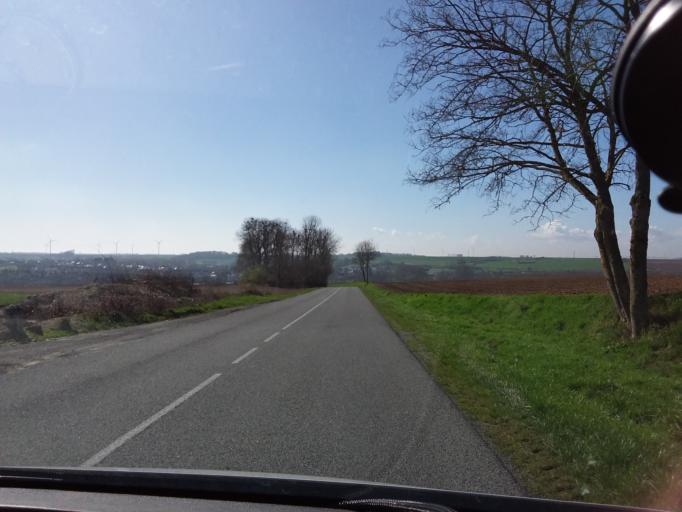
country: FR
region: Picardie
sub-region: Departement de l'Aisne
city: Montcornet
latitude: 49.7076
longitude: 4.0149
